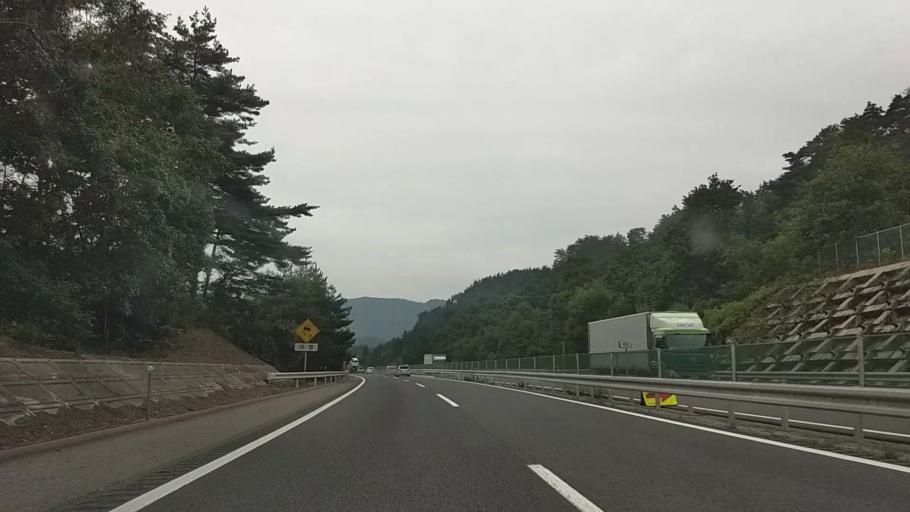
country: JP
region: Nagano
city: Hotaka
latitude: 36.4030
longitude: 138.0009
